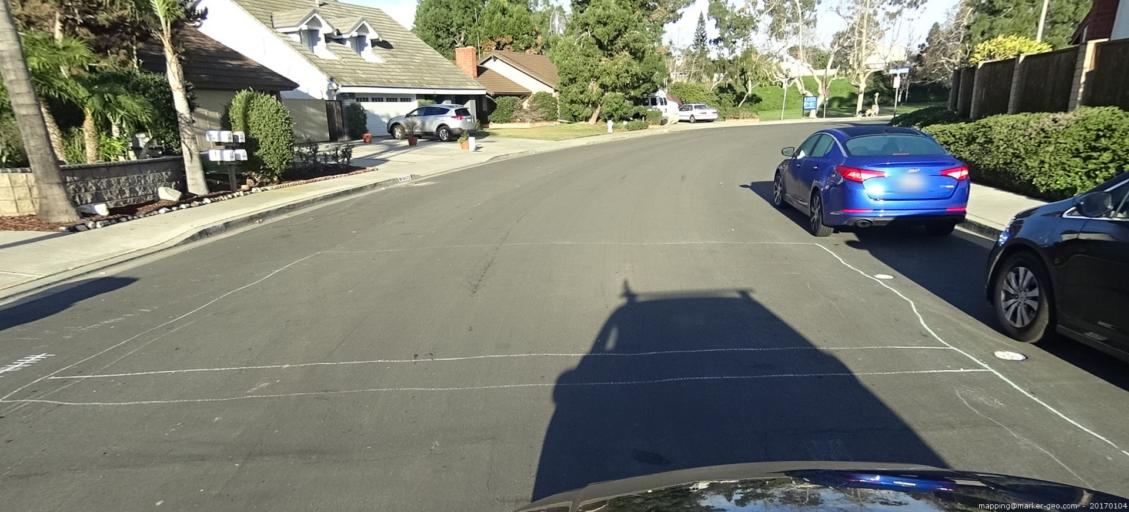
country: US
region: California
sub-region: Orange County
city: Dana Point
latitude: 33.4805
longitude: -117.7041
